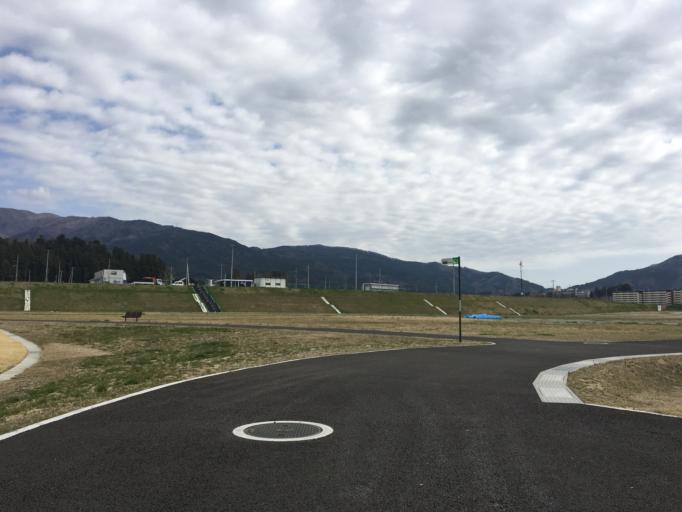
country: JP
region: Iwate
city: Ofunato
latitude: 39.0112
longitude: 141.6364
